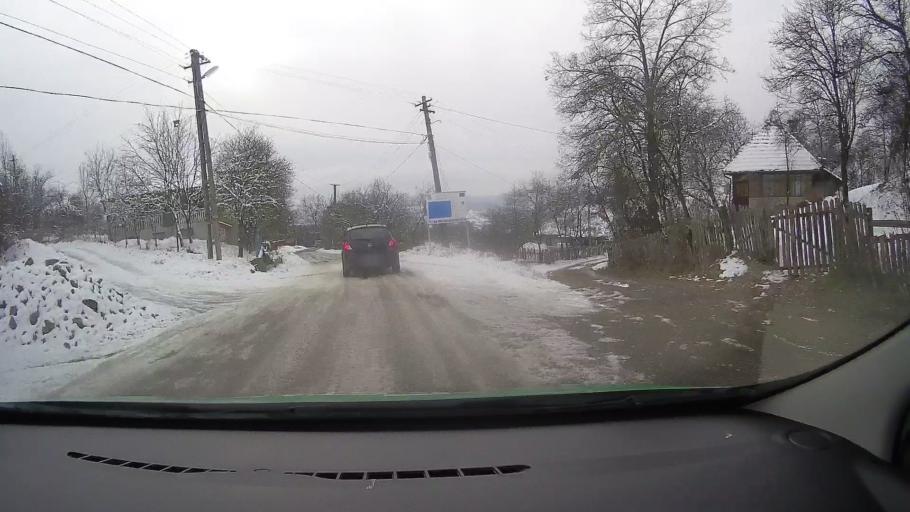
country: RO
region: Alba
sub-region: Comuna Almasu Mare
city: Almasu Mare
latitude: 46.0881
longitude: 23.1294
